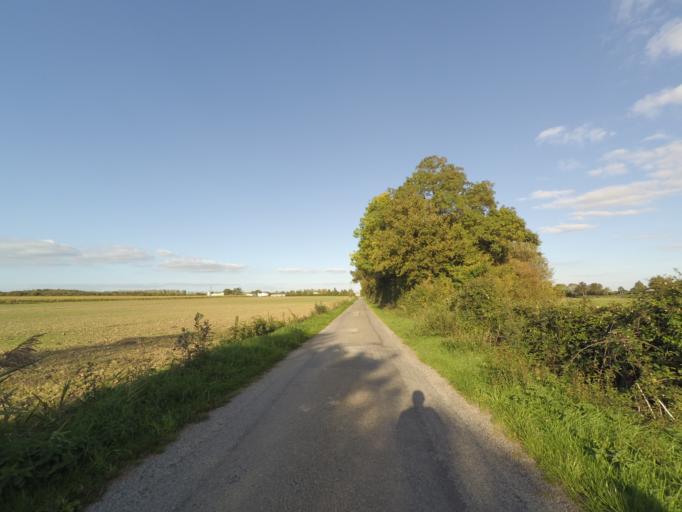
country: FR
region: Pays de la Loire
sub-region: Departement de la Loire-Atlantique
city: Chemere
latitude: 47.1363
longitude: -1.9162
